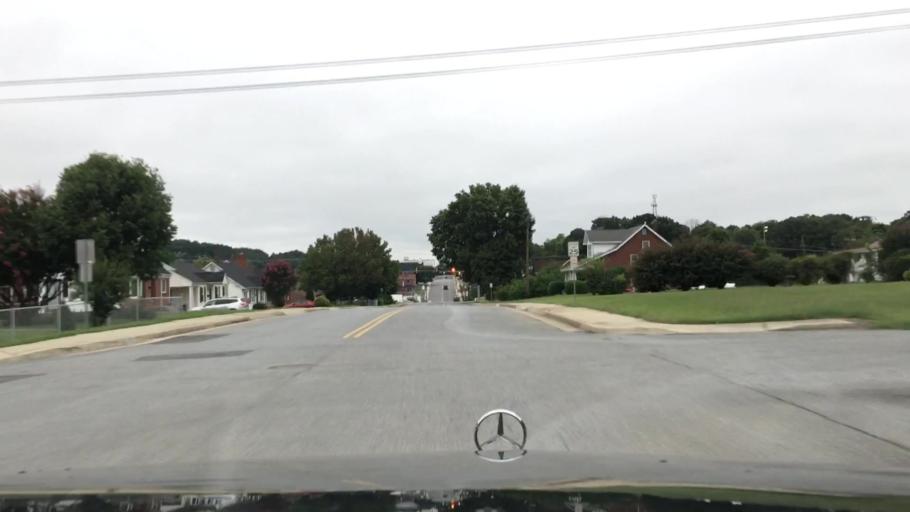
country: US
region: Virginia
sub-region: Campbell County
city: Altavista
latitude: 37.1135
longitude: -79.2850
